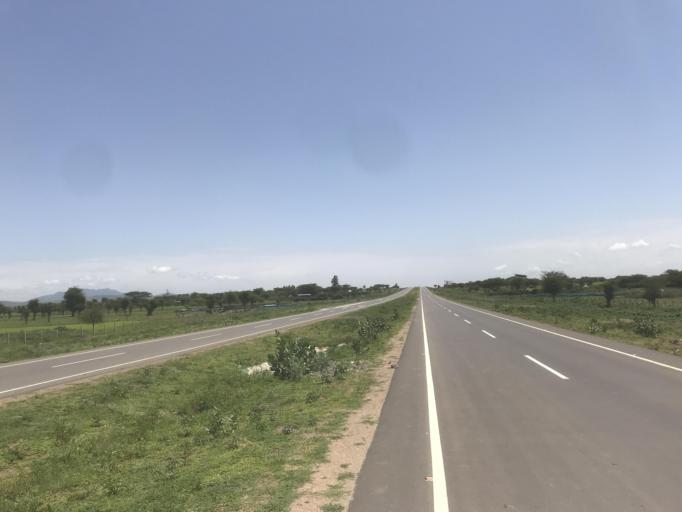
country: ET
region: Oromiya
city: Mojo
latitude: 8.3718
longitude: 38.9974
